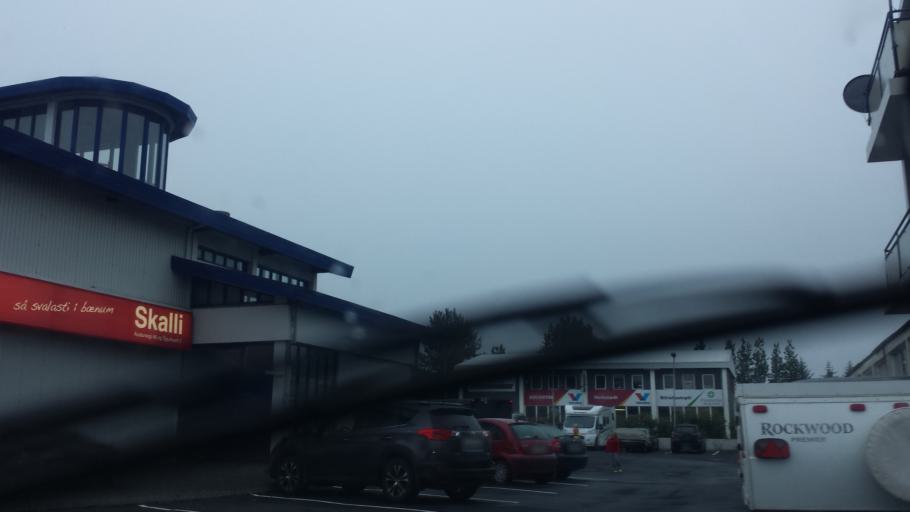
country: IS
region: South
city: Selfoss
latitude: 63.9369
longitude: -20.9888
